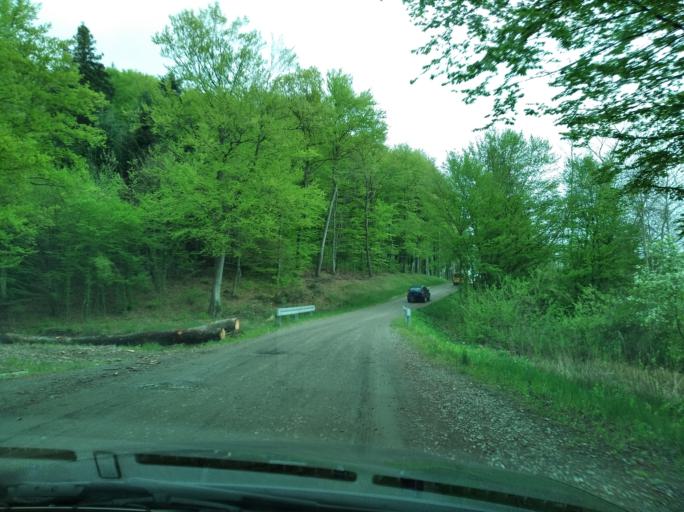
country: PL
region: Subcarpathian Voivodeship
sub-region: Powiat sanocki
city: Sanok
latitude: 49.5671
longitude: 22.2307
